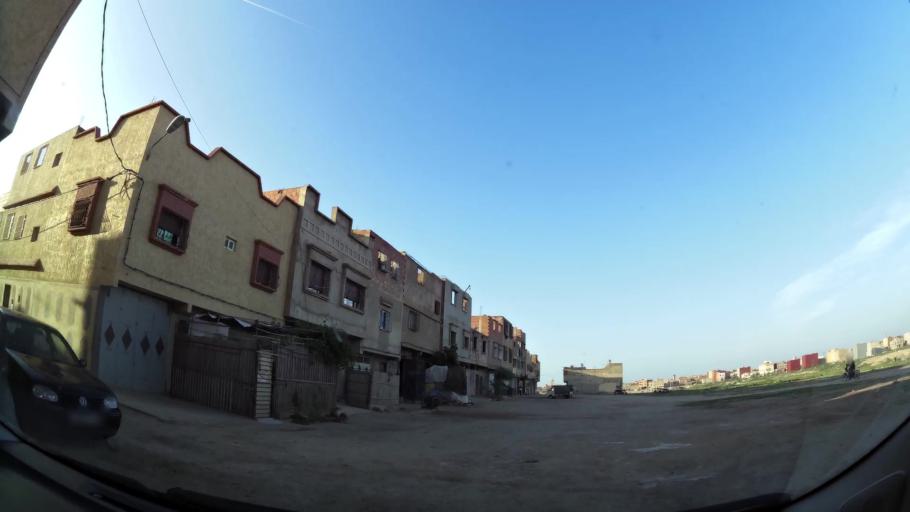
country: MA
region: Oriental
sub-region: Oujda-Angad
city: Oujda
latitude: 34.7076
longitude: -1.9068
